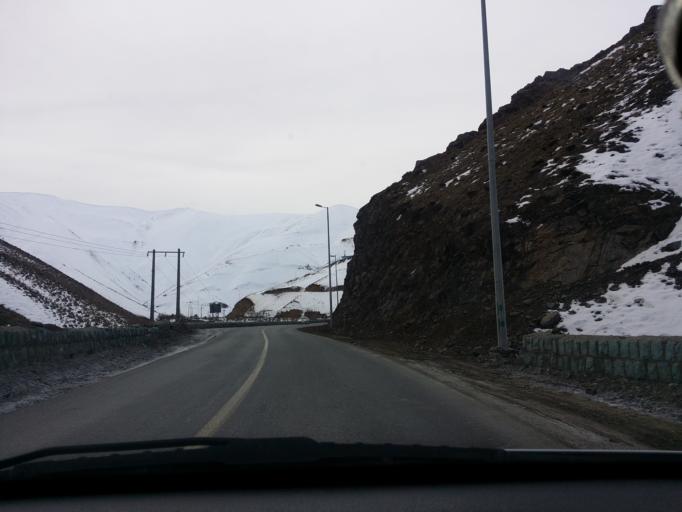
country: IR
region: Tehran
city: Tajrish
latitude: 36.1677
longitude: 51.3163
